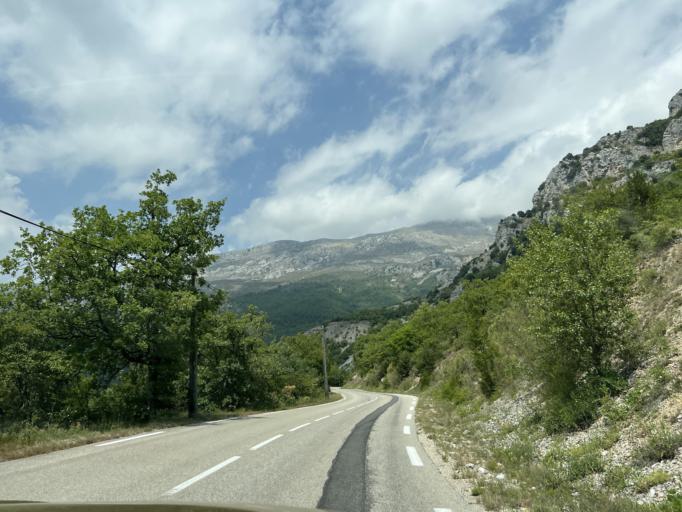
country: FR
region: Provence-Alpes-Cote d'Azur
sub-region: Departement des Alpes-Maritimes
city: Tourrettes-sur-Loup
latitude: 43.7842
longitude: 6.9754
